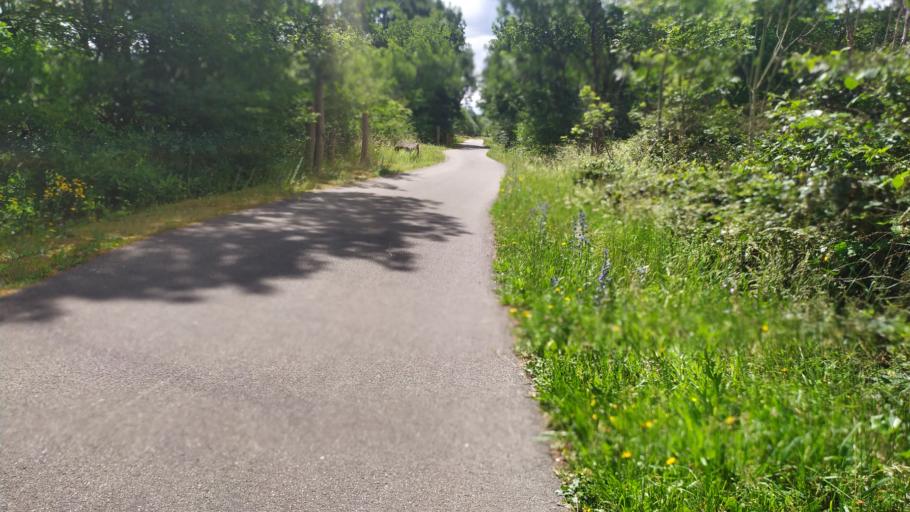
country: BE
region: Wallonia
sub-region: Province de Namur
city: Houyet
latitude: 50.1675
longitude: 5.0527
